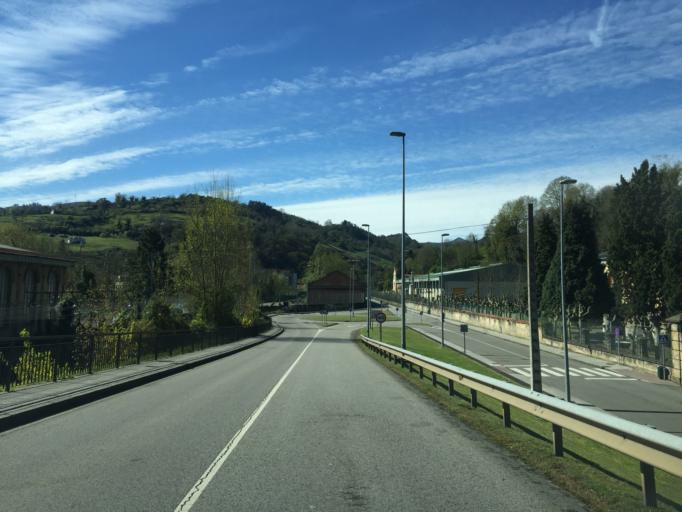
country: ES
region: Asturias
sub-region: Province of Asturias
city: Castandiello
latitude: 43.3518
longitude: -5.9682
